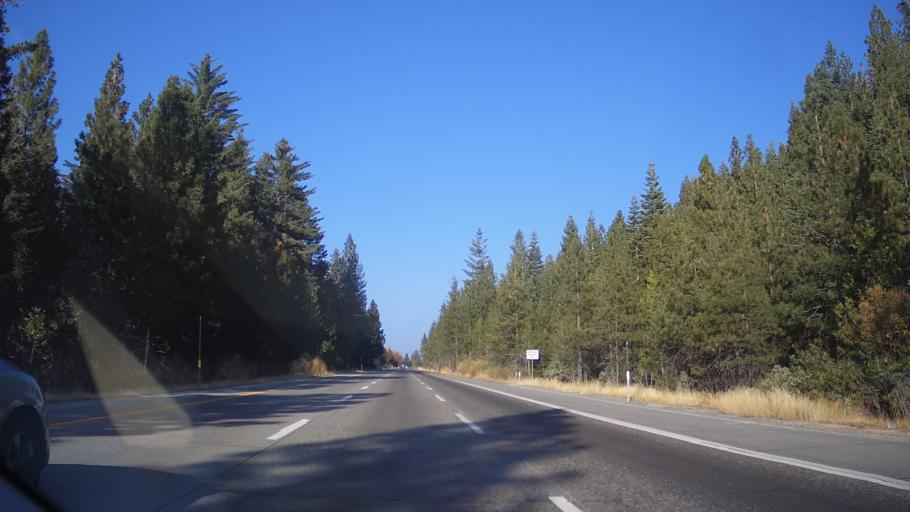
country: US
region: California
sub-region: Placer County
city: Foresthill
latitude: 39.2615
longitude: -120.7287
